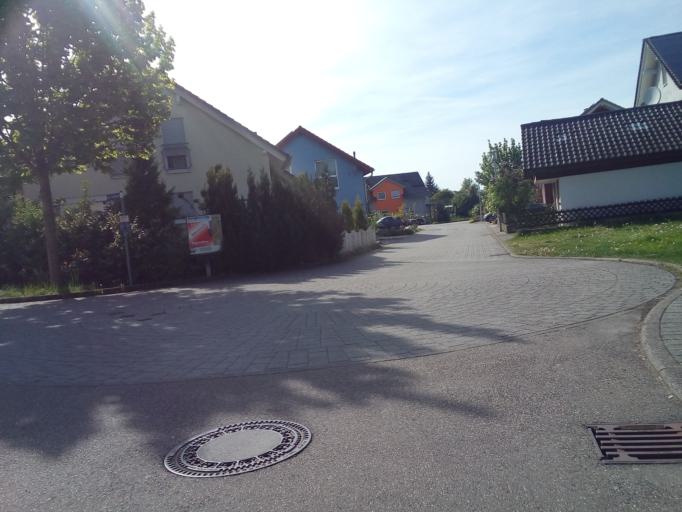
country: DE
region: Baden-Wuerttemberg
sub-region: Karlsruhe Region
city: Lichtenau
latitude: 48.7201
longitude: 8.0018
